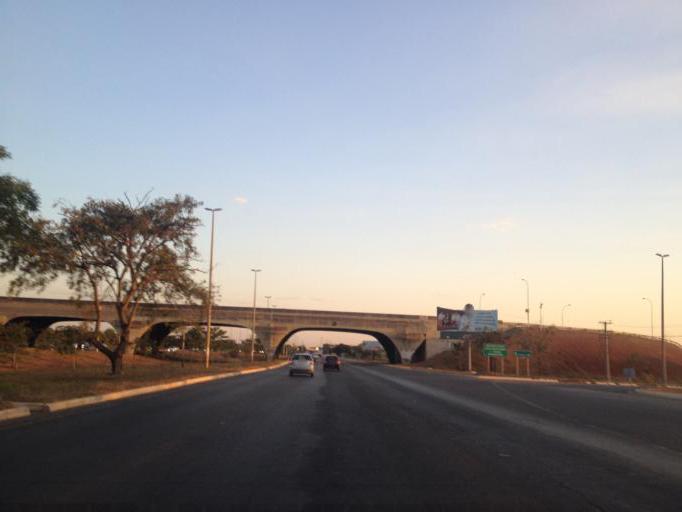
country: BR
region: Federal District
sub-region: Brasilia
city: Brasilia
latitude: -15.7733
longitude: -47.9374
